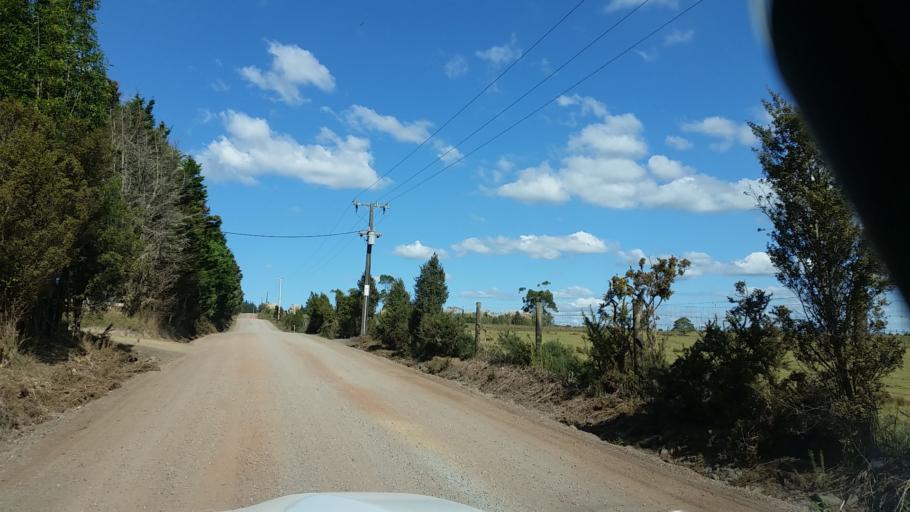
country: NZ
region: Northland
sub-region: Whangarei
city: Whangarei
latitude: -35.5812
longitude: 174.3107
